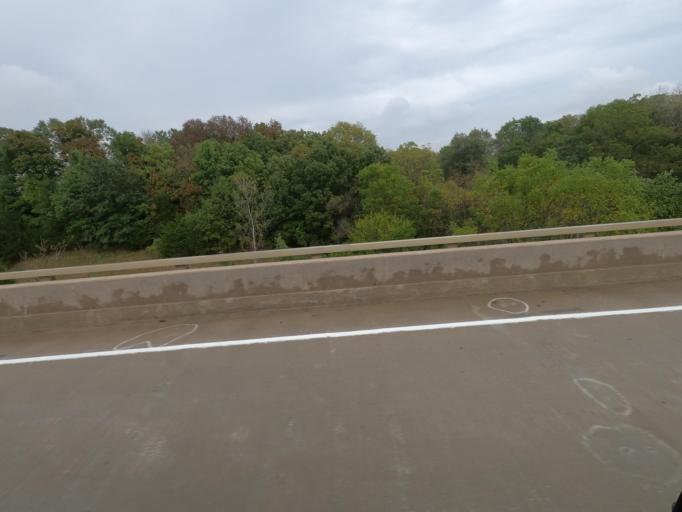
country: US
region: Iowa
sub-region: Van Buren County
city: Keosauqua
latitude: 40.8219
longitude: -91.9465
